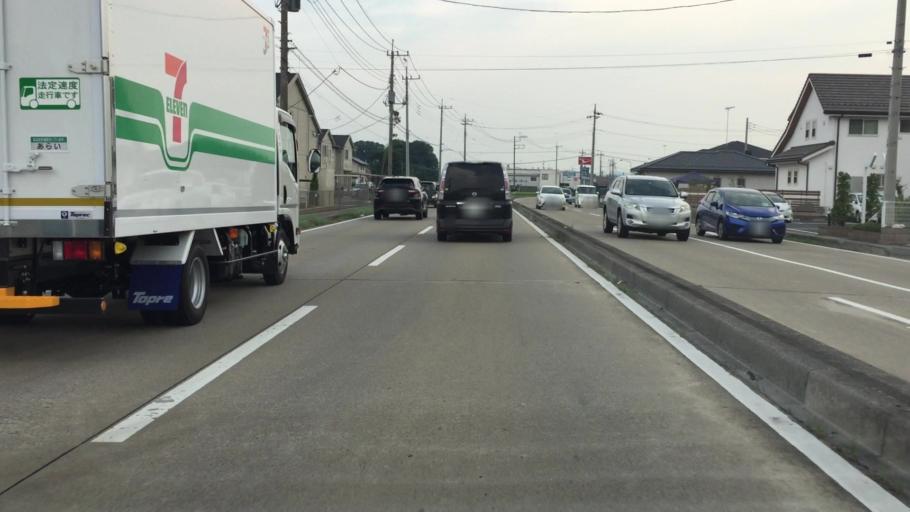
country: JP
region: Tochigi
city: Tochigi
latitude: 36.3453
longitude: 139.7011
